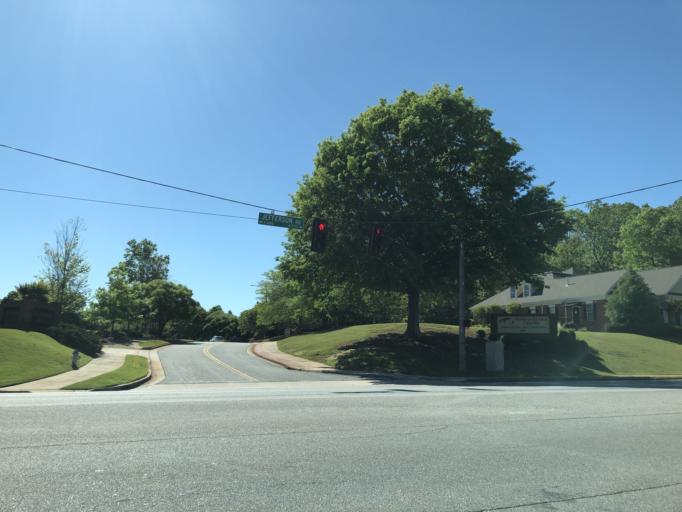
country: US
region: Georgia
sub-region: Clarke County
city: Country Club Estates
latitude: 33.9767
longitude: -83.4144
